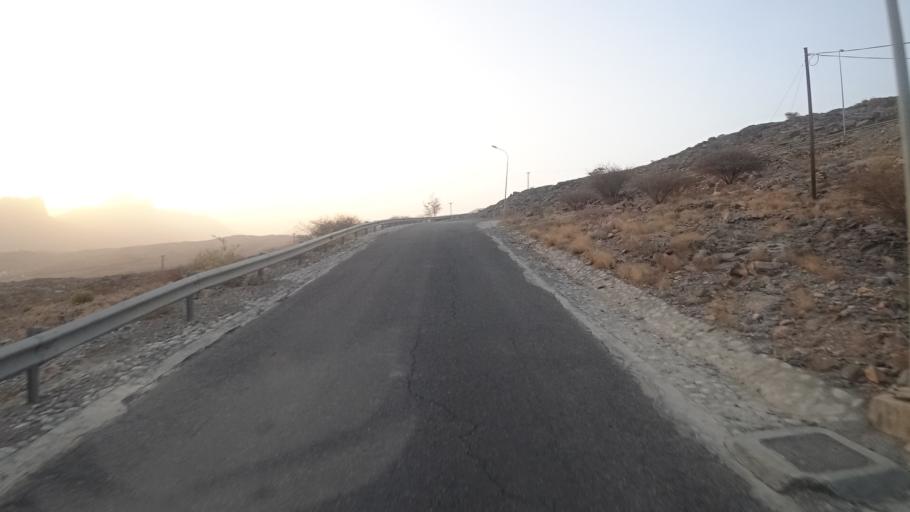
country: OM
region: Muhafazat ad Dakhiliyah
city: Bahla'
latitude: 23.1309
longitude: 57.3040
